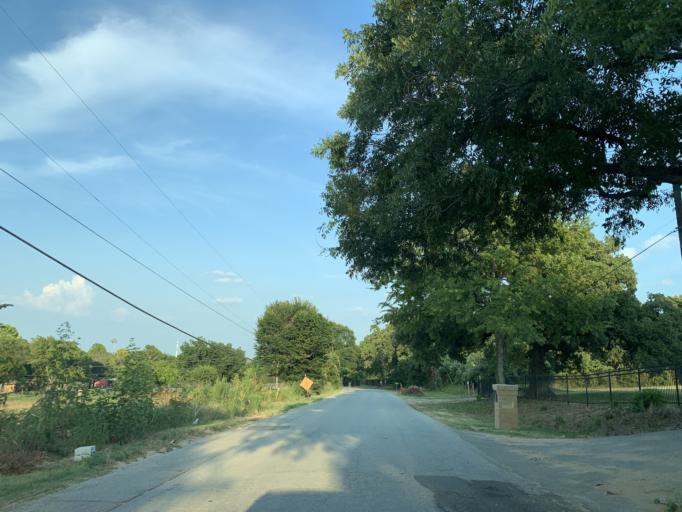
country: US
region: Texas
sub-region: Tarrant County
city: Hurst
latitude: 32.7808
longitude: -97.1901
